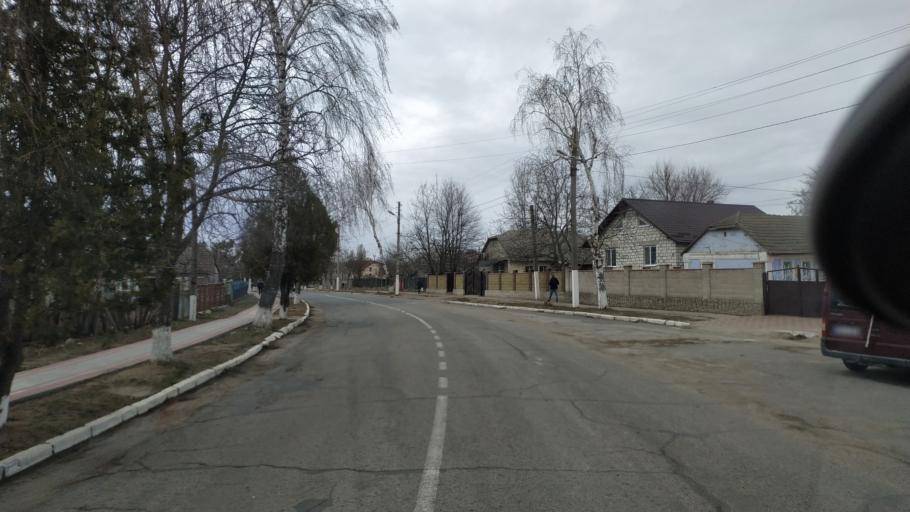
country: MD
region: Telenesti
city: Cocieri
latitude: 47.3065
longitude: 29.1118
